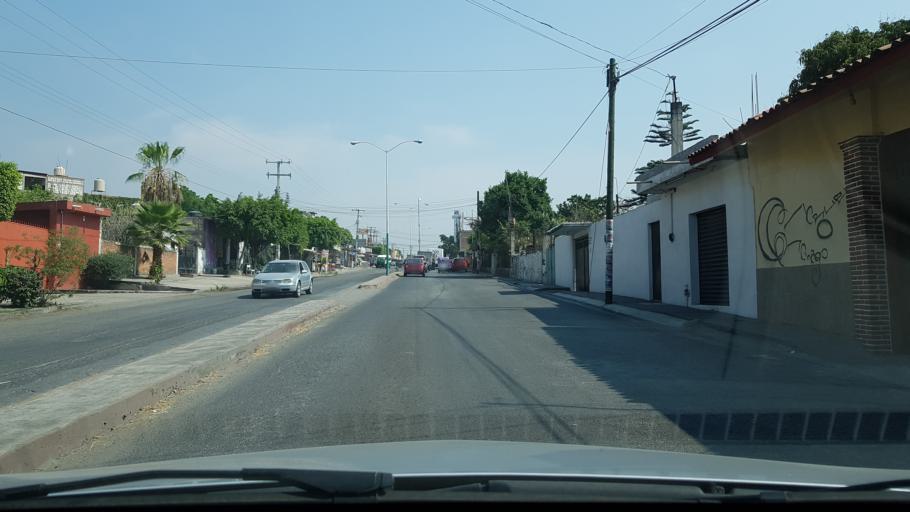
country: MX
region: Morelos
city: Zacatepec
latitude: 18.6707
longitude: -99.1856
